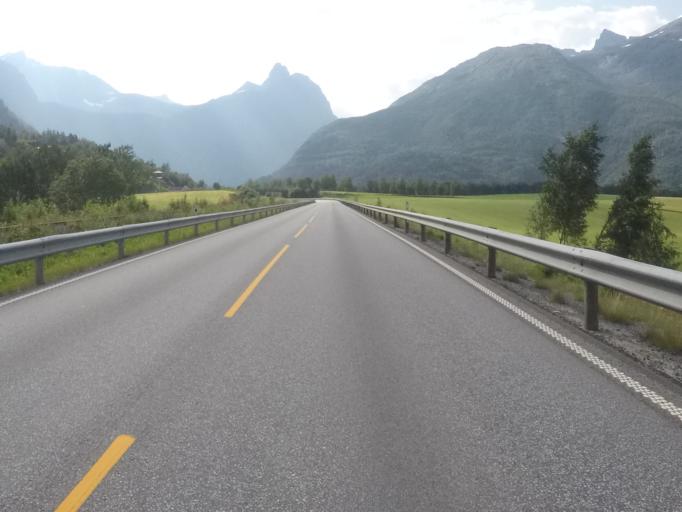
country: NO
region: More og Romsdal
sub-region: Rauma
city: Andalsnes
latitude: 62.5428
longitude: 7.7197
